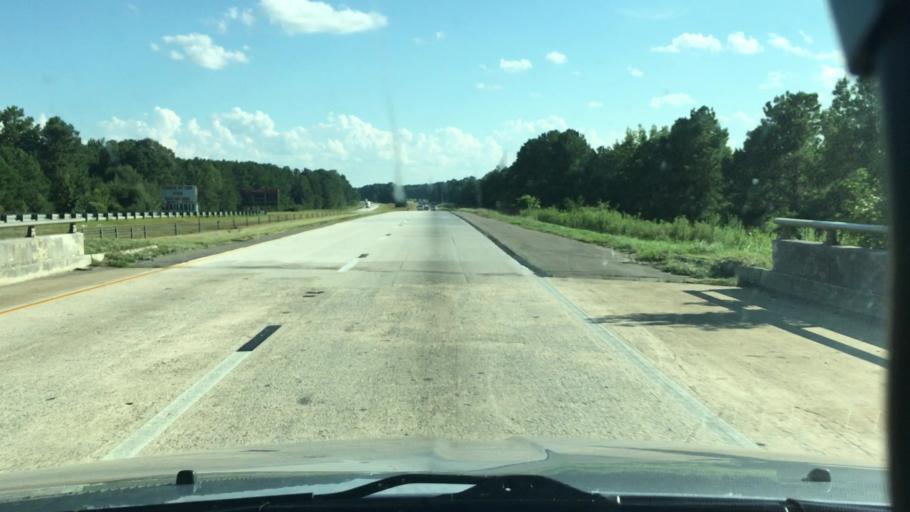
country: US
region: South Carolina
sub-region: Dorchester County
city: Saint George
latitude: 33.1739
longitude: -80.6156
